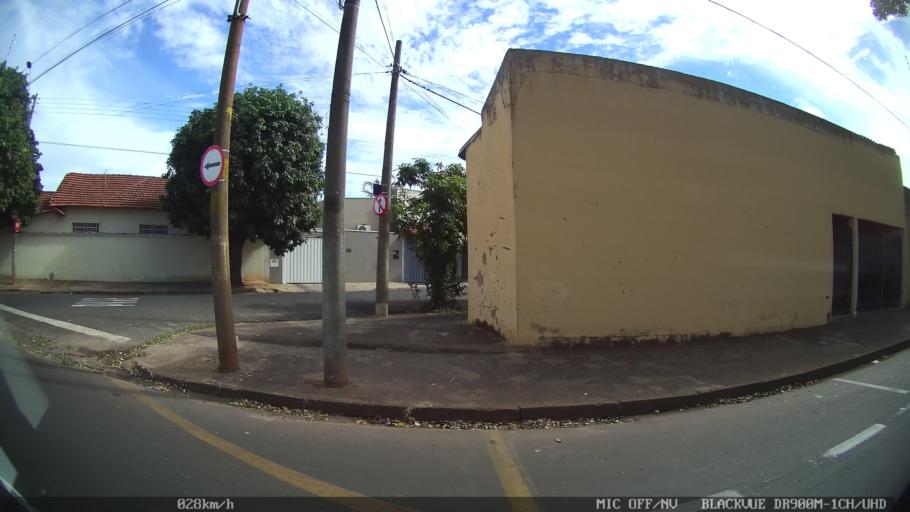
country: BR
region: Sao Paulo
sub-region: Catanduva
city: Catanduva
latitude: -21.1290
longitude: -48.9534
